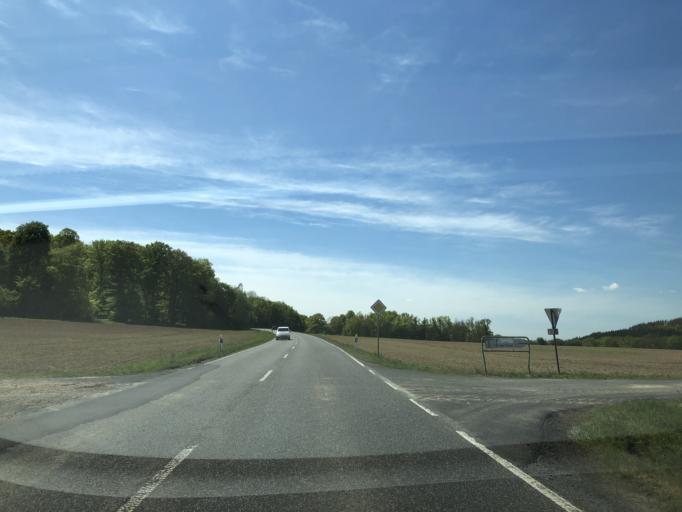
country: DE
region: Hesse
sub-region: Regierungsbezirk Kassel
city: Homberg
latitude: 51.0604
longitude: 9.4417
